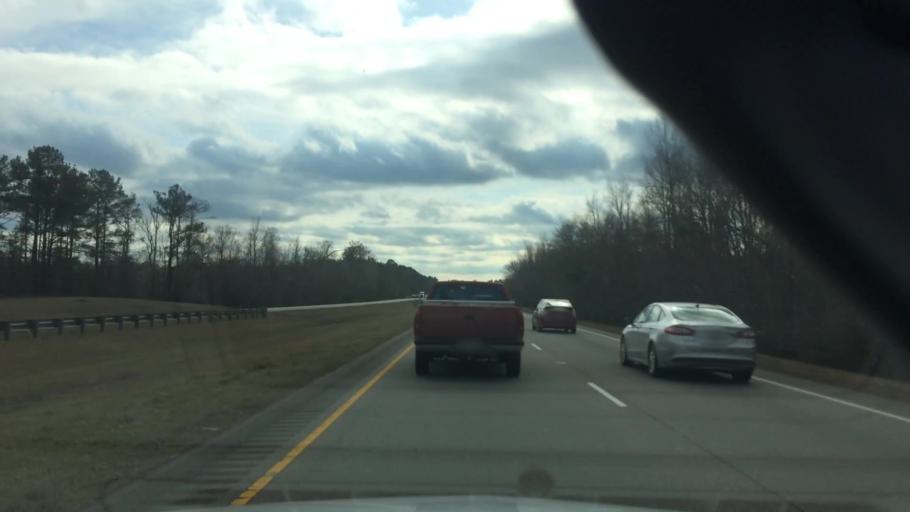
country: US
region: North Carolina
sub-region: Brunswick County
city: Leland
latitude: 34.1631
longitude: -78.0903
